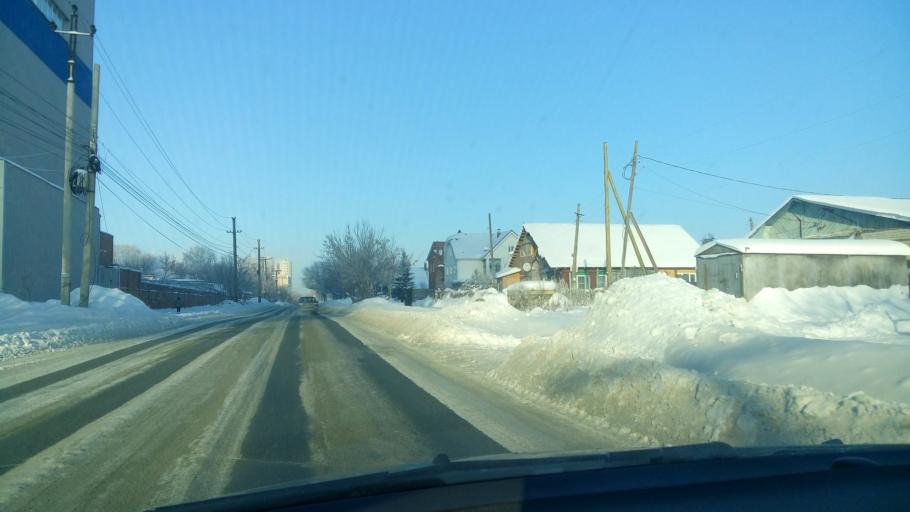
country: RU
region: Chelyabinsk
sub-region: Gorod Chelyabinsk
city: Chelyabinsk
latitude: 55.1277
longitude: 61.3815
